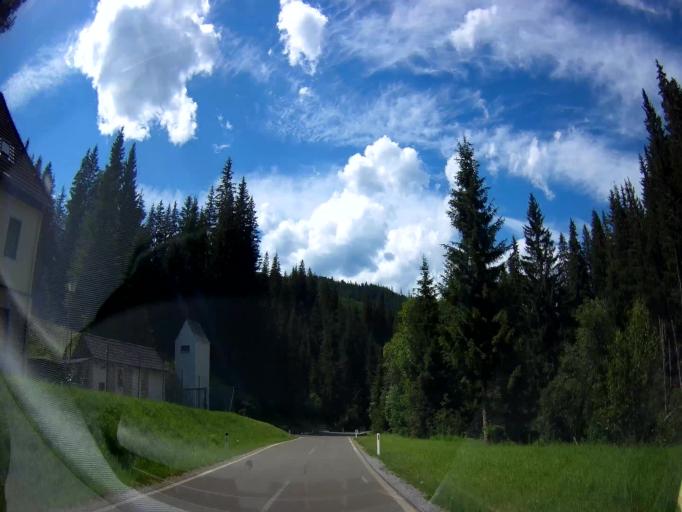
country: AT
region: Styria
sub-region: Politischer Bezirk Murau
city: Stadl an der Mur
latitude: 47.0159
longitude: 14.0055
